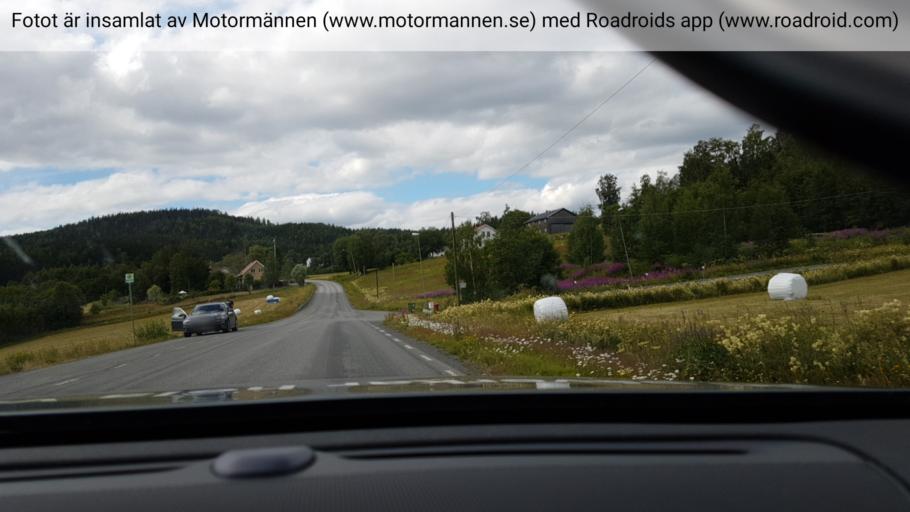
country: SE
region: Vaesternorrland
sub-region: Kramfors Kommun
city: Nordingra
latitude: 62.9389
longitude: 18.2426
